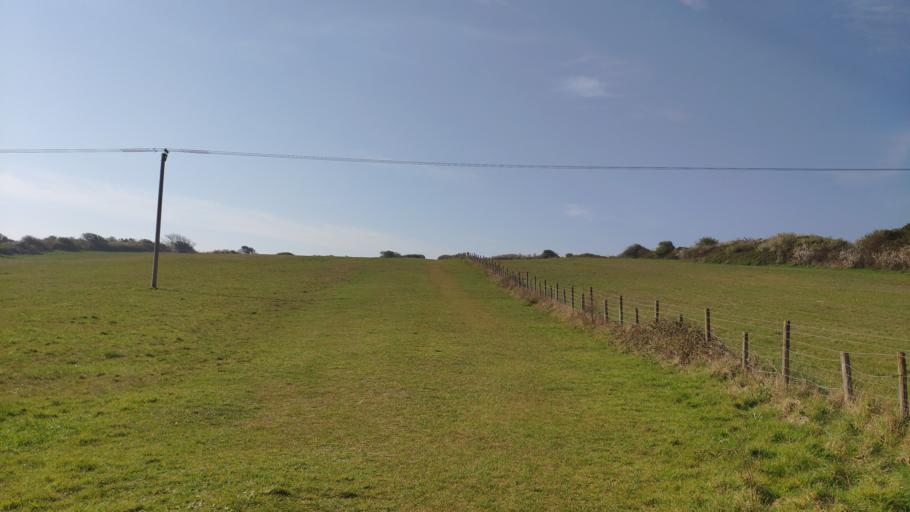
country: GB
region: England
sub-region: Dorset
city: Swanage
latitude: 50.5997
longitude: -1.9666
